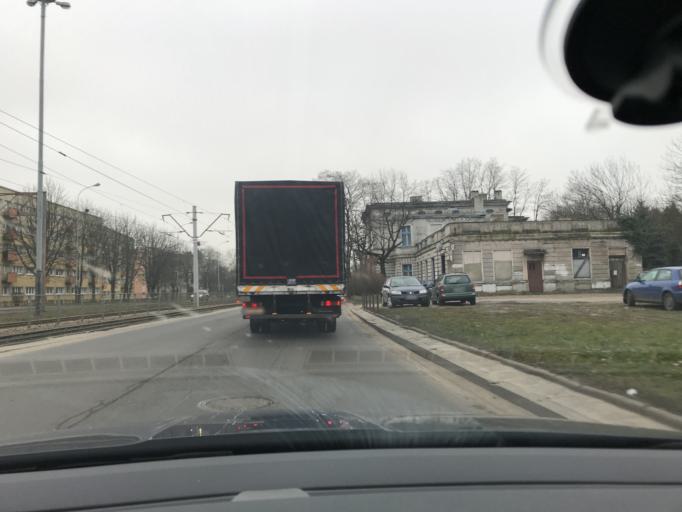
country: PL
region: Lodz Voivodeship
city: Lodz
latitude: 51.7308
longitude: 19.4521
